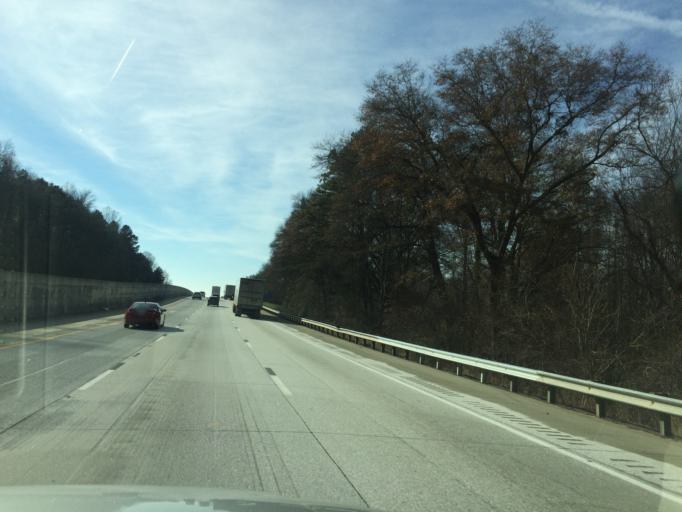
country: US
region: South Carolina
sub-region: Anderson County
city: Northlake
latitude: 34.6050
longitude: -82.6409
